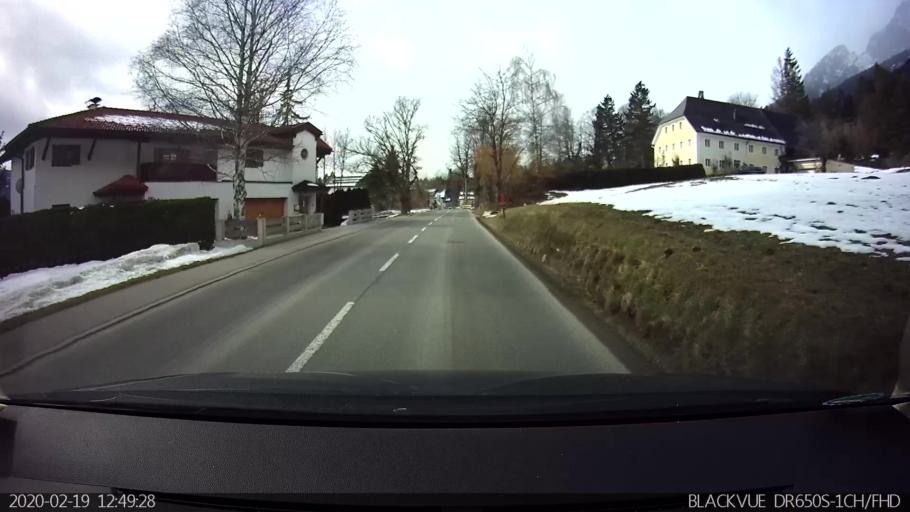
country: AT
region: Tyrol
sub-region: Politischer Bezirk Innsbruck Land
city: Gnadenwald
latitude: 47.3208
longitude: 11.5562
